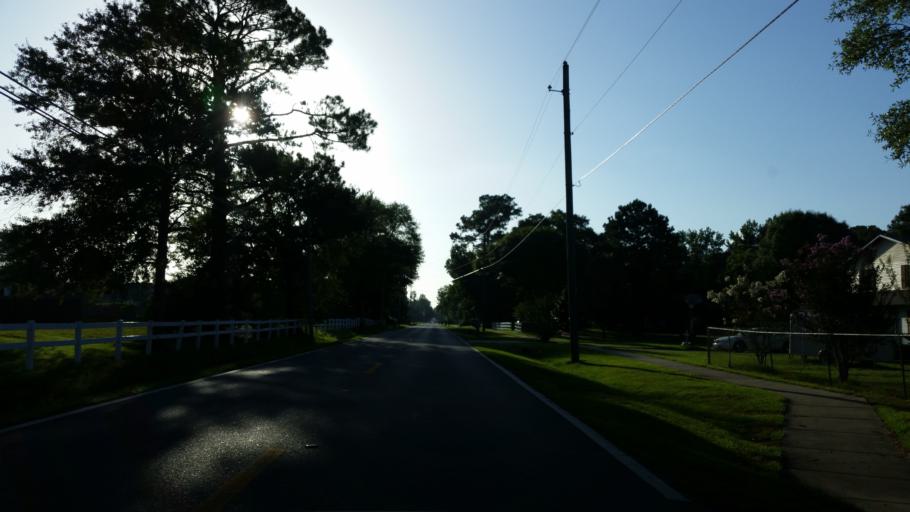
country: US
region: Florida
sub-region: Escambia County
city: Bellview
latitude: 30.4689
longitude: -87.3218
